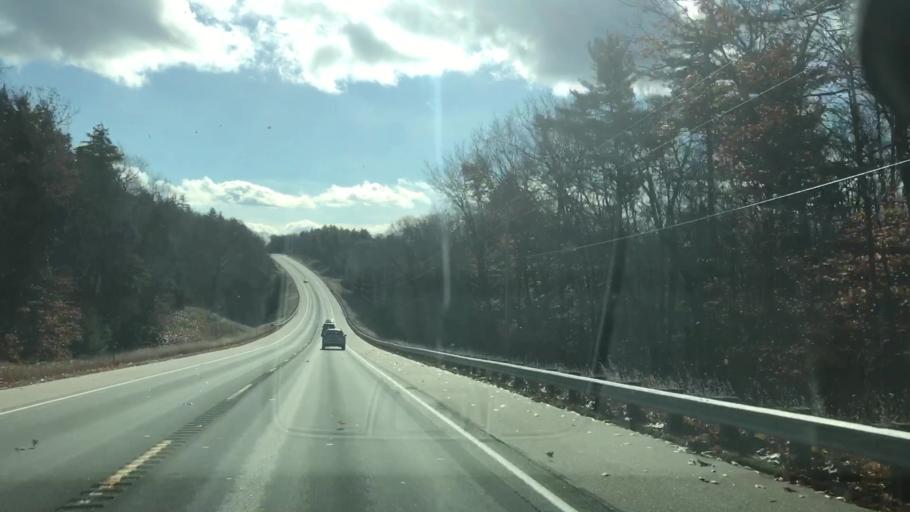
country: US
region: New Hampshire
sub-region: Strafford County
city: New Durham
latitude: 43.4803
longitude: -71.2276
